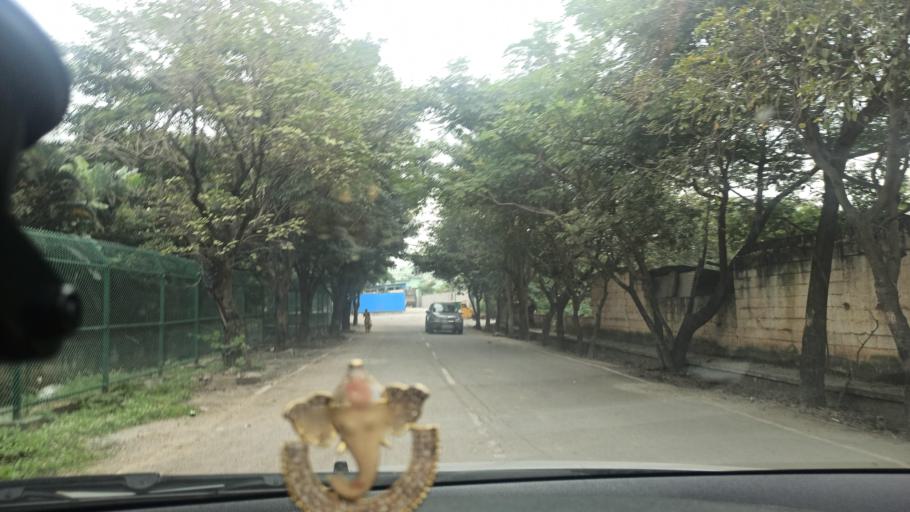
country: IN
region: Karnataka
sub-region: Bangalore Urban
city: Bangalore
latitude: 12.9156
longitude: 77.6424
